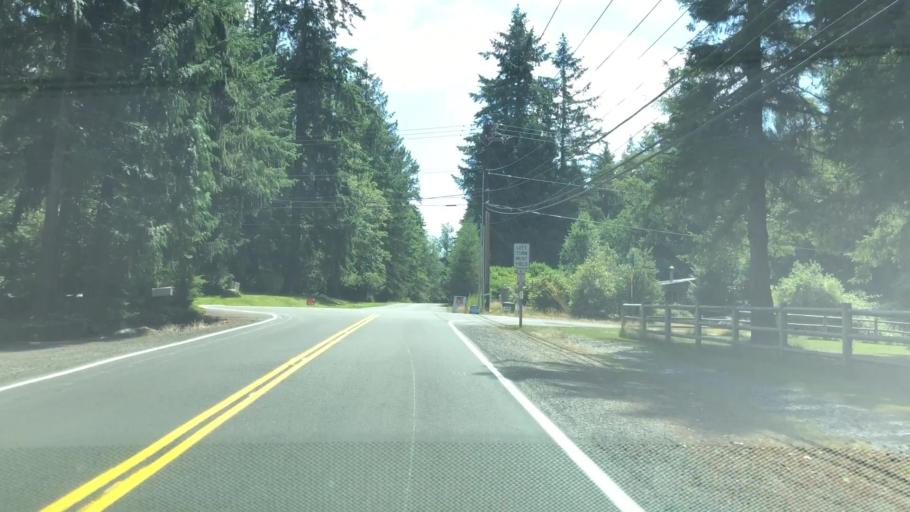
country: US
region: Washington
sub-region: King County
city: Cottage Lake
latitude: 47.7481
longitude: -122.0535
